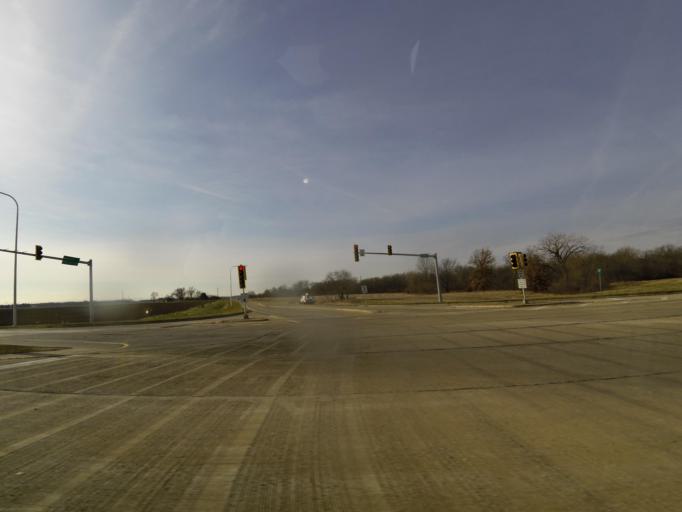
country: US
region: Illinois
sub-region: De Witt County
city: Clinton
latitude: 40.1277
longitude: -88.9663
